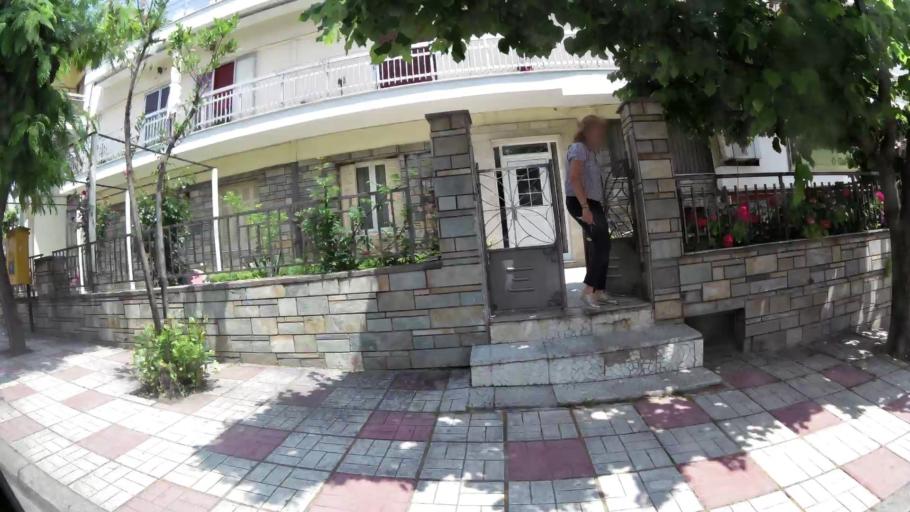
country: GR
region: West Macedonia
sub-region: Nomos Kozanis
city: Kozani
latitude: 40.2957
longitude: 21.7851
